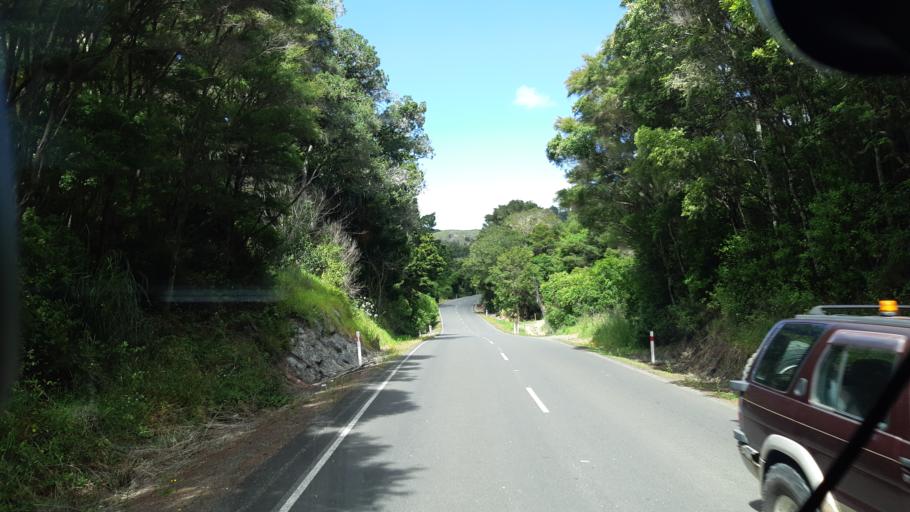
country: NZ
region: Northland
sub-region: Far North District
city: Taipa
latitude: -35.2567
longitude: 173.5338
